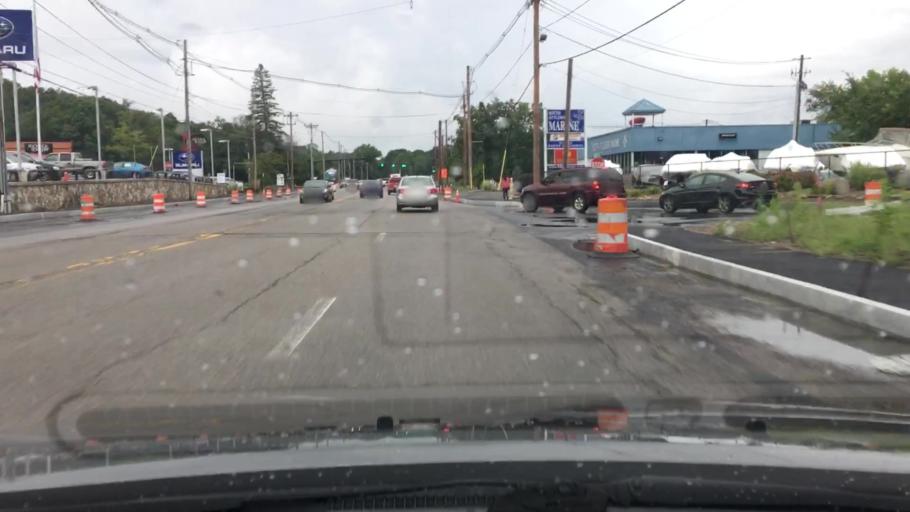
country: US
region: Massachusetts
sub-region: Norfolk County
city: Plainville
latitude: 41.9642
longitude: -71.3398
